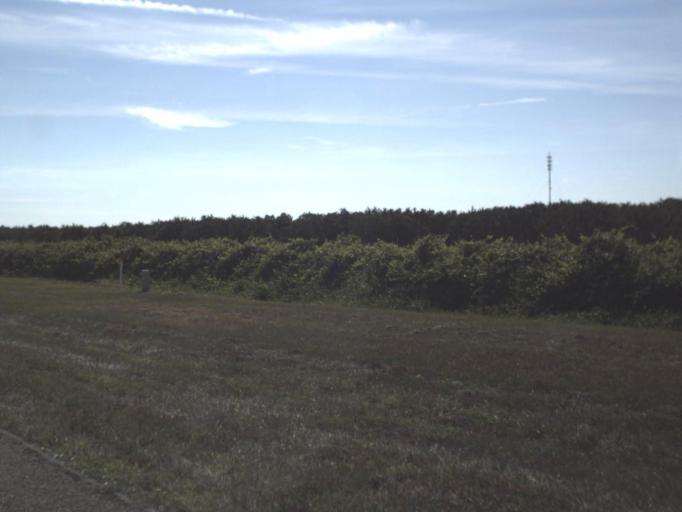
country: US
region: Florida
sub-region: Highlands County
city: Placid Lakes
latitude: 27.0737
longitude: -81.3360
